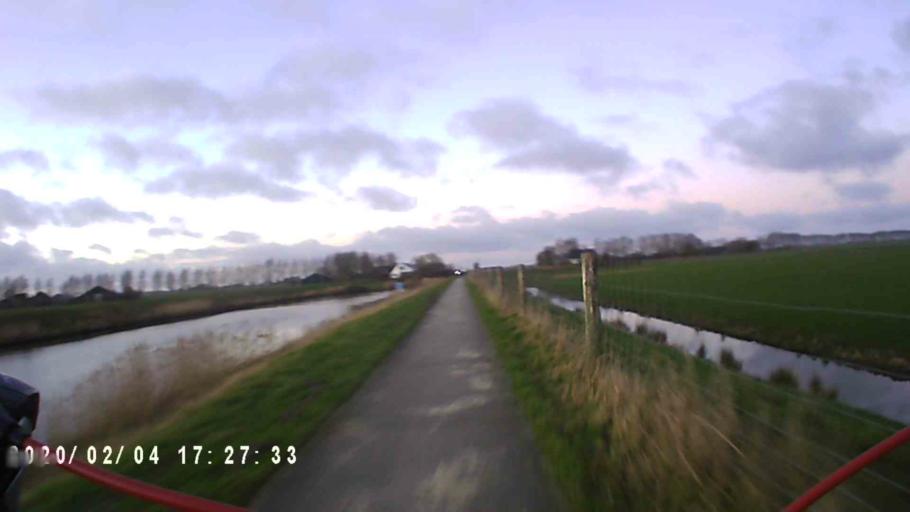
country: NL
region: Groningen
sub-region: Gemeente Zuidhorn
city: Aduard
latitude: 53.2662
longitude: 6.5074
